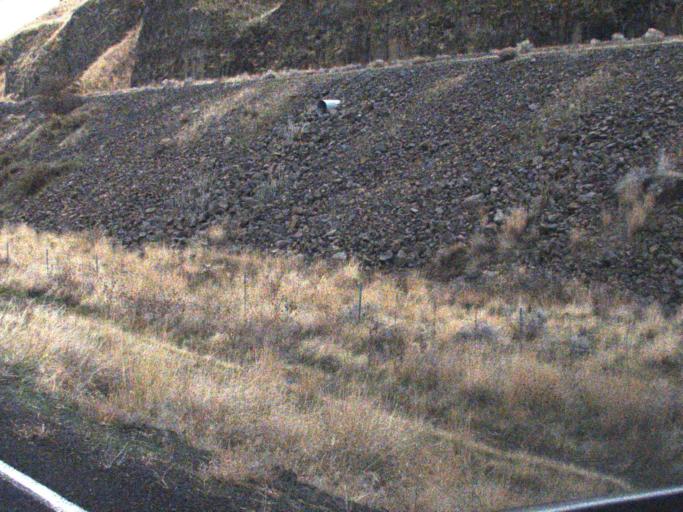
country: US
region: Washington
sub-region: Walla Walla County
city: Waitsburg
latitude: 46.5600
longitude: -118.1819
